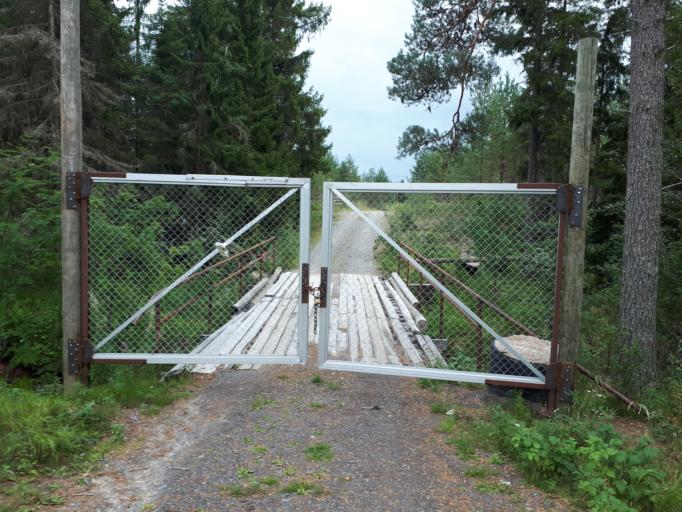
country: FI
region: Northern Ostrobothnia
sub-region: Oulunkaari
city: Ii
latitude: 65.3022
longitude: 25.4171
